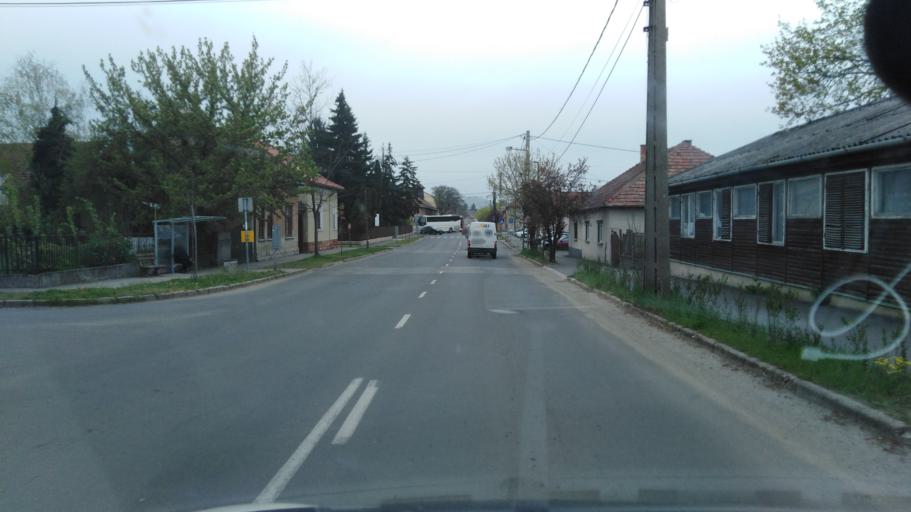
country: HU
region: Nograd
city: Balassagyarmat
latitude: 48.0724
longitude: 19.2964
